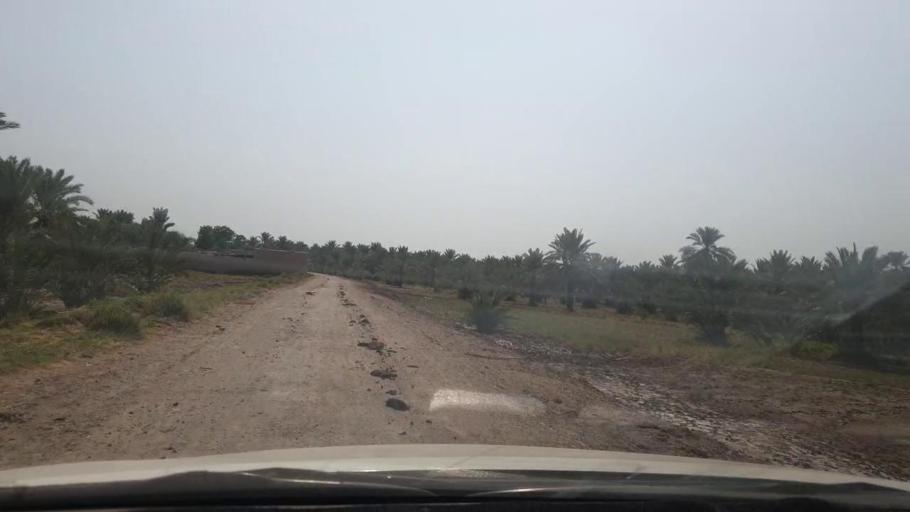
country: PK
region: Sindh
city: Khairpur
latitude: 27.5634
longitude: 68.8423
